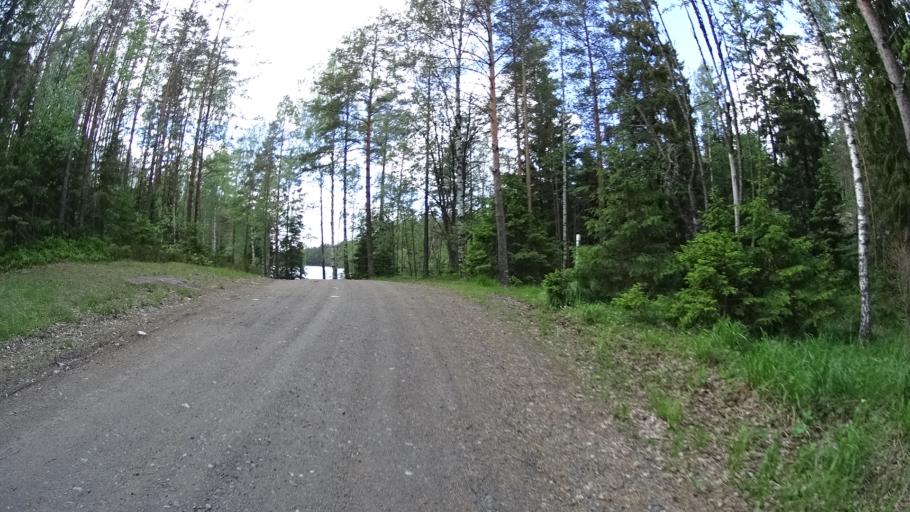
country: FI
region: Varsinais-Suomi
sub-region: Salo
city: Kisko
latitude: 60.1802
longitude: 23.5248
